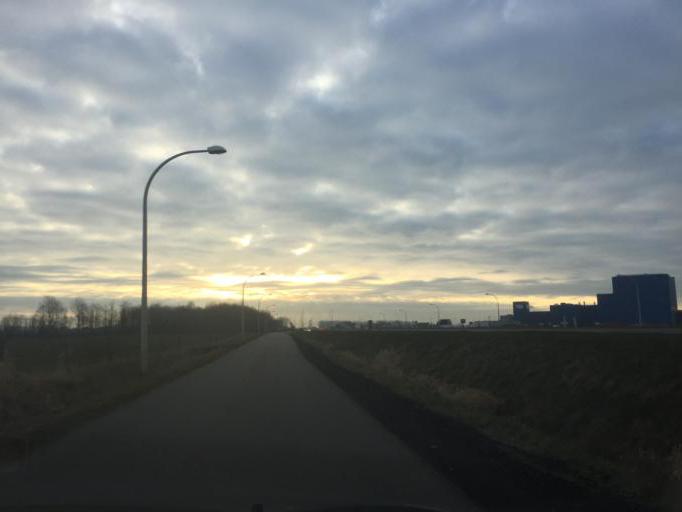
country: BE
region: Flanders
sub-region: Provincie West-Vlaanderen
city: Ardooie
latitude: 50.9778
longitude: 3.1576
